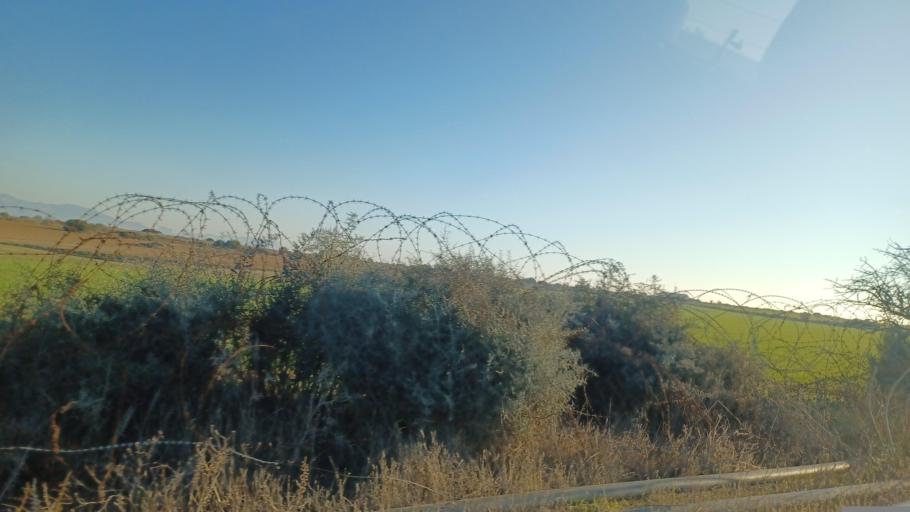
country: CY
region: Lefkosia
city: Kato Deftera
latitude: 35.1467
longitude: 33.2690
